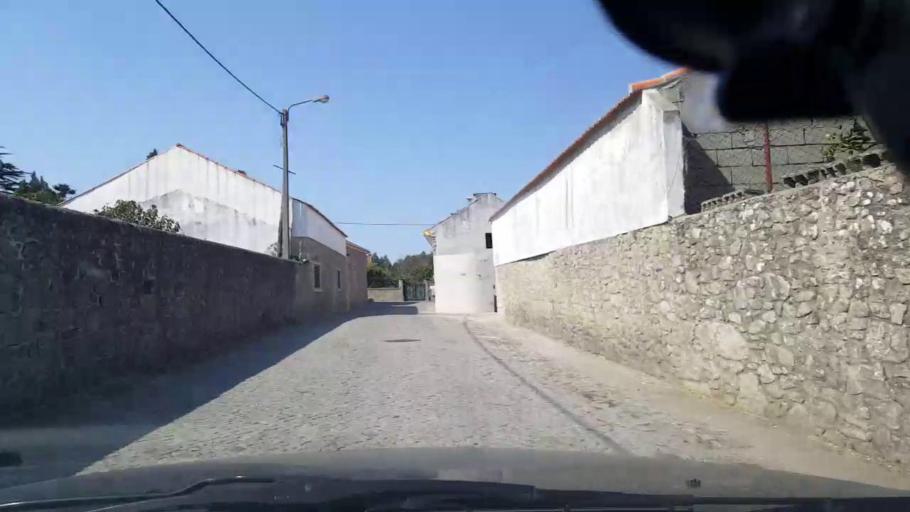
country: PT
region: Porto
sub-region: Povoa de Varzim
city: Pedroso
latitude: 41.3872
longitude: -8.7063
